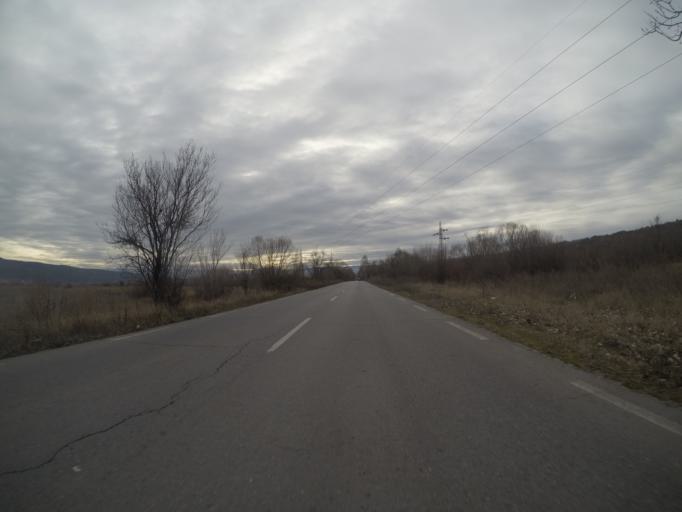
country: BG
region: Kyustendil
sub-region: Obshtina Rila
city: Rila
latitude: 42.1101
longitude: 23.1060
